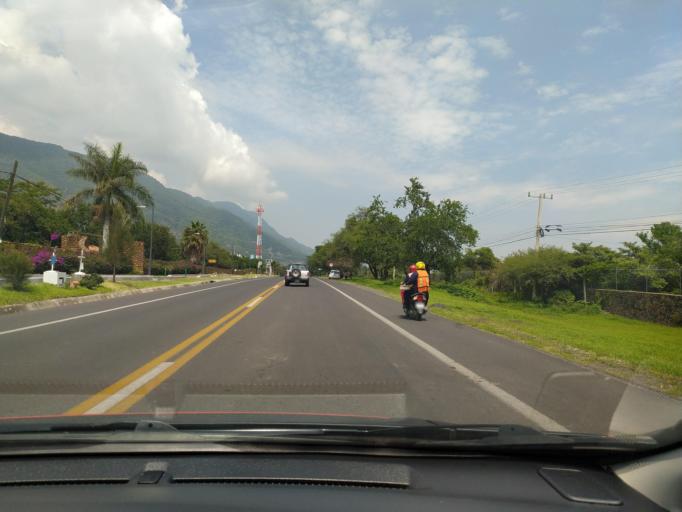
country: MX
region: Jalisco
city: Jocotepec
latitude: 20.2927
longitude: -103.3974
